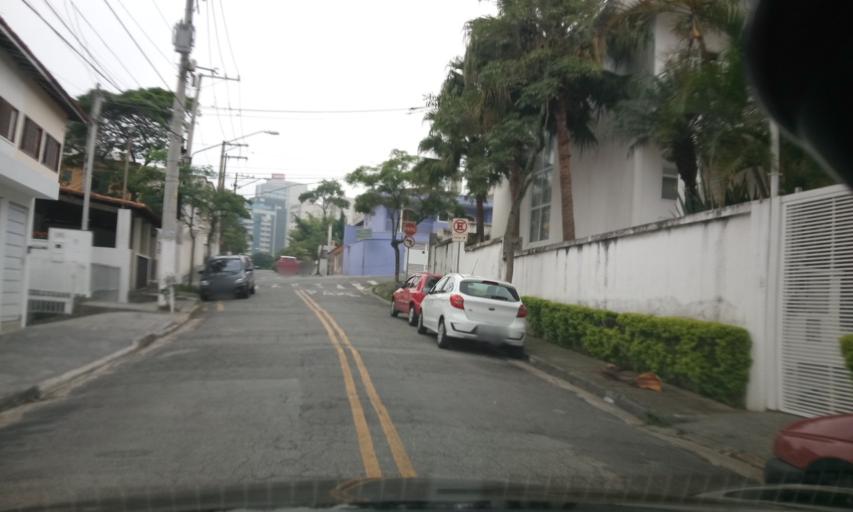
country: BR
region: Sao Paulo
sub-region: Sao Bernardo Do Campo
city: Sao Bernardo do Campo
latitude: -23.6822
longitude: -46.5567
